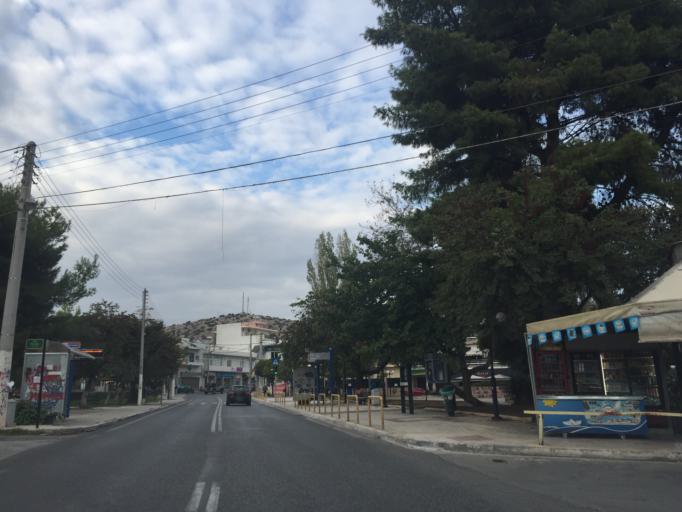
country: GR
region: Attica
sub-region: Nomarchia Anatolikis Attikis
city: Vari
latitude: 37.8305
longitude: 23.8031
